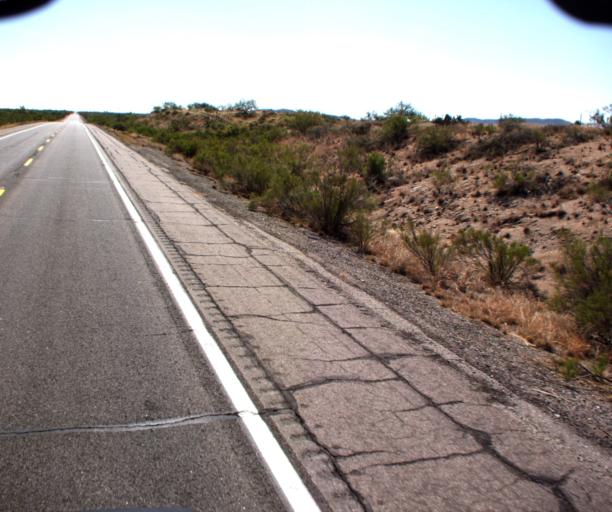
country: US
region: Arizona
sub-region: Pinal County
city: Oracle
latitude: 32.6132
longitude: -110.8358
